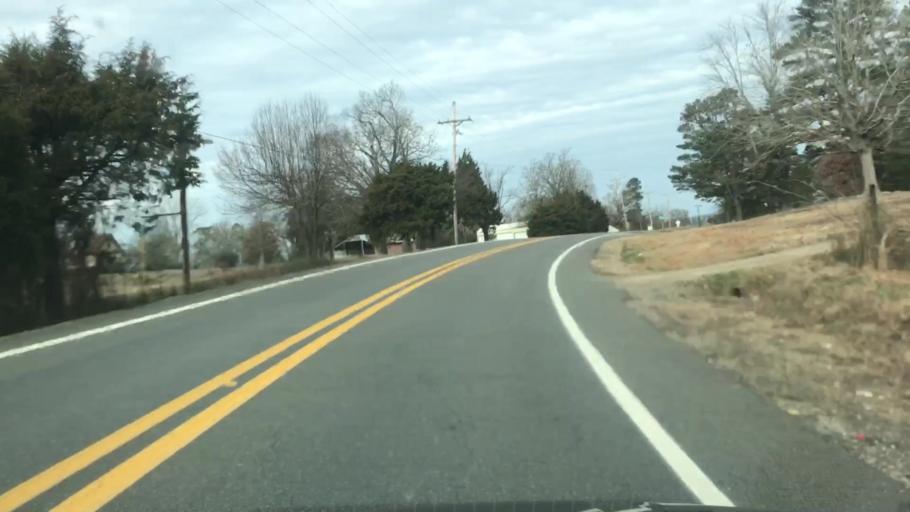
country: US
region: Arkansas
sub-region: Montgomery County
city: Mount Ida
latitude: 34.6251
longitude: -93.7300
